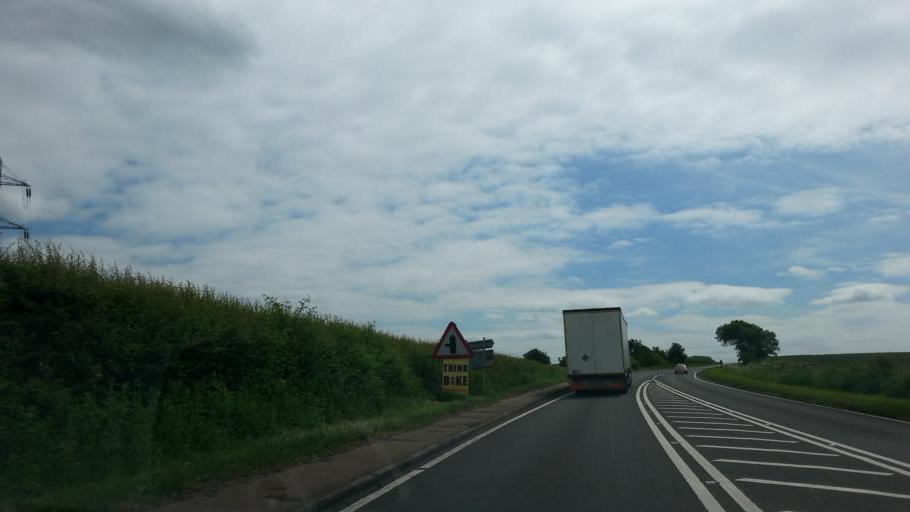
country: GB
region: England
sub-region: Nottinghamshire
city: Cotgrave
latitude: 52.8865
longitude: -1.0740
